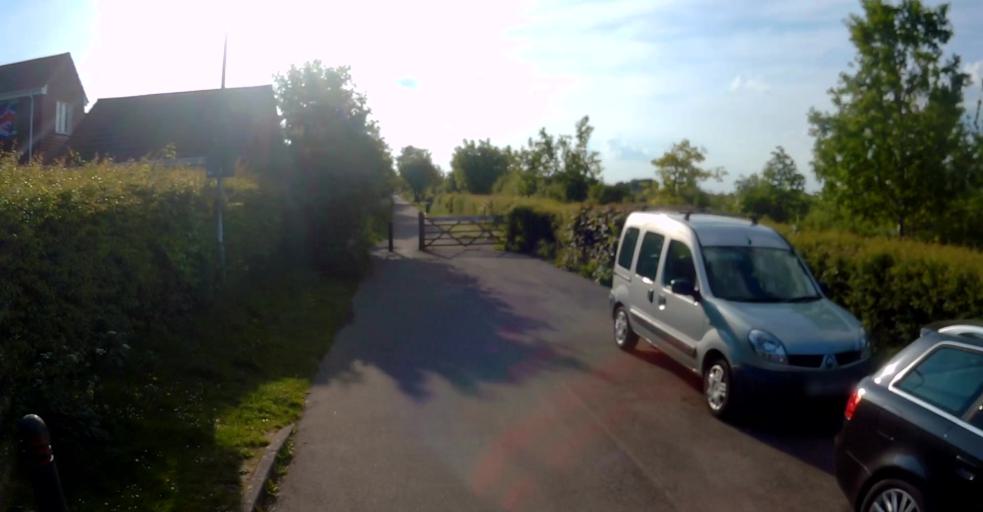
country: GB
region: England
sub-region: Hampshire
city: Basingstoke
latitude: 51.2292
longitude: -1.1362
